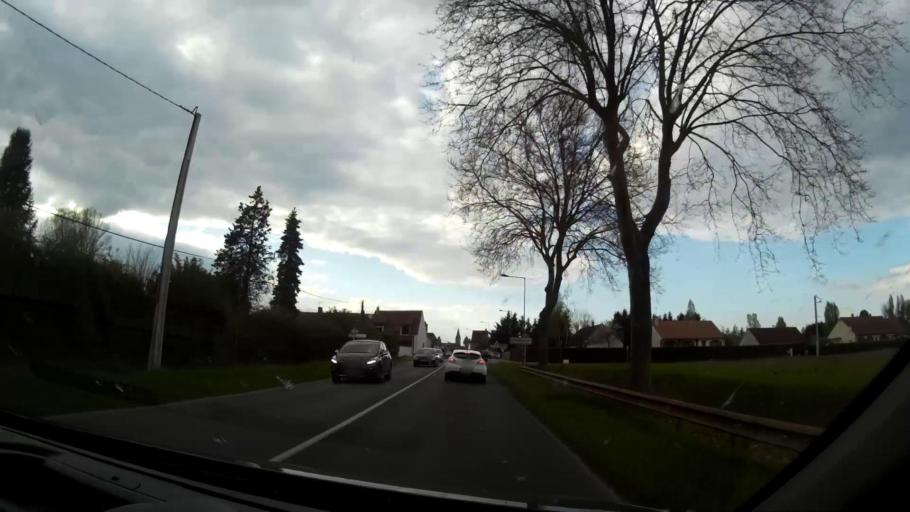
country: FR
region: Centre
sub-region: Departement du Loir-et-Cher
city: Cormeray
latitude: 47.4858
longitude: 1.4105
